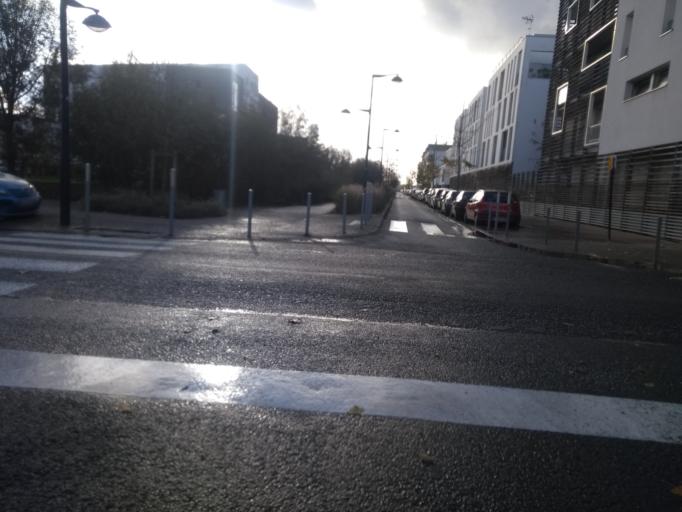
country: FR
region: Aquitaine
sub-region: Departement de la Gironde
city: Floirac
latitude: 44.8273
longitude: -0.5290
